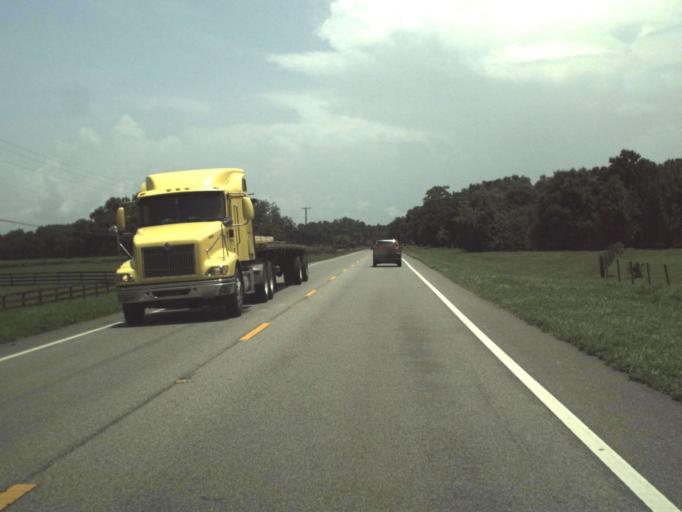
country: US
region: Florida
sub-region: Sumter County
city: Lake Panasoffkee
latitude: 28.7802
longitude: -82.0676
